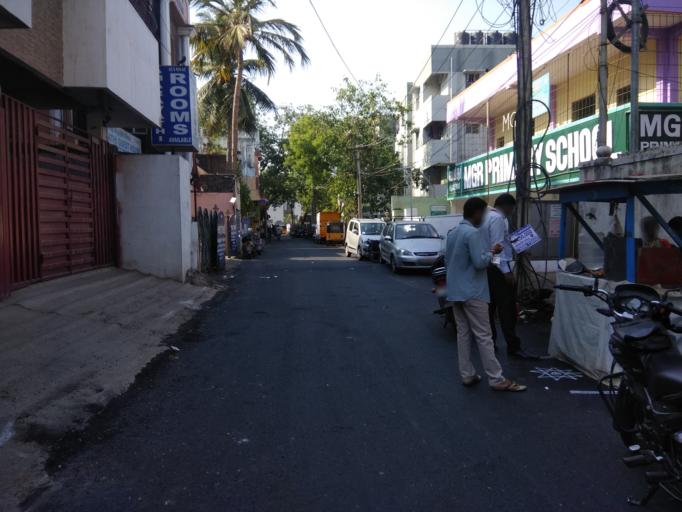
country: IN
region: Tamil Nadu
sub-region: Chennai
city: Chetput
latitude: 13.0489
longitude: 80.2114
